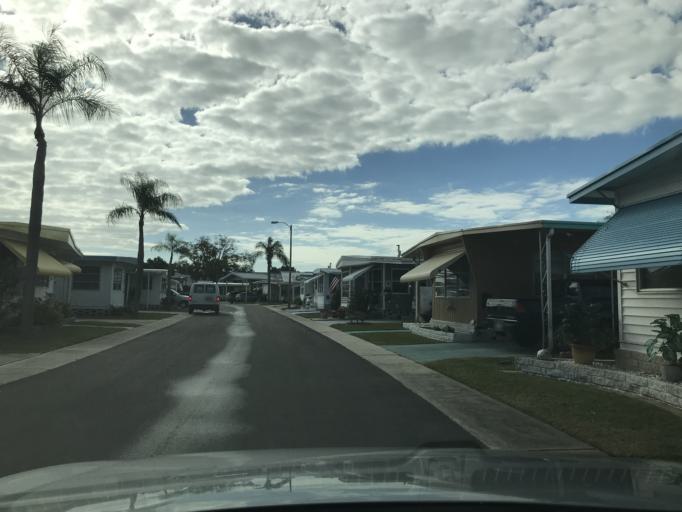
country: US
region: Florida
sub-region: Pinellas County
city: Largo
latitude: 27.9244
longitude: -82.7908
